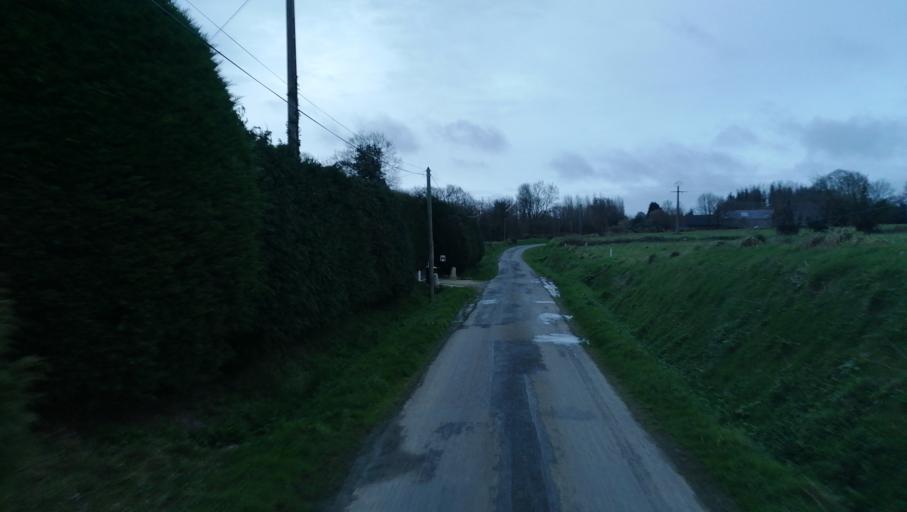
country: FR
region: Brittany
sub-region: Departement des Cotes-d'Armor
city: Goudelin
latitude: 48.5786
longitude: -3.0540
